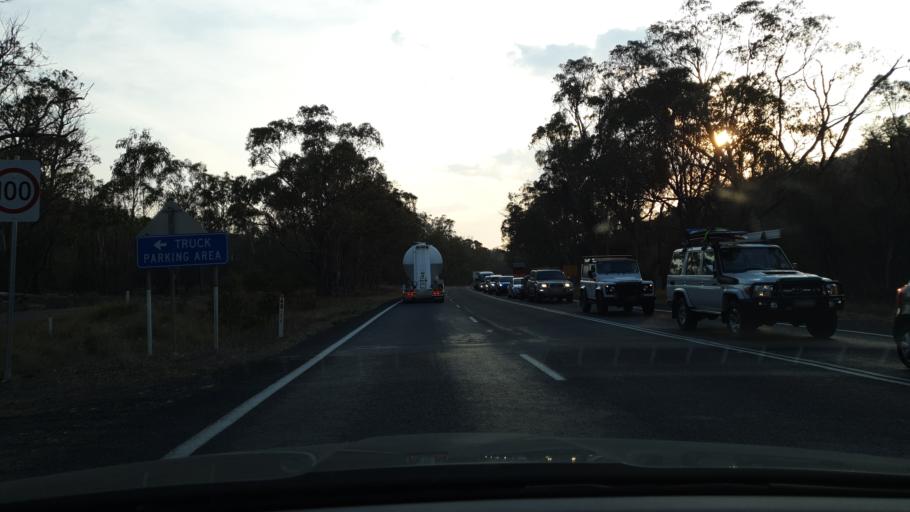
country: AU
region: New South Wales
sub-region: Glen Innes Severn
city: Glen Innes
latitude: -29.3247
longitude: 151.9156
